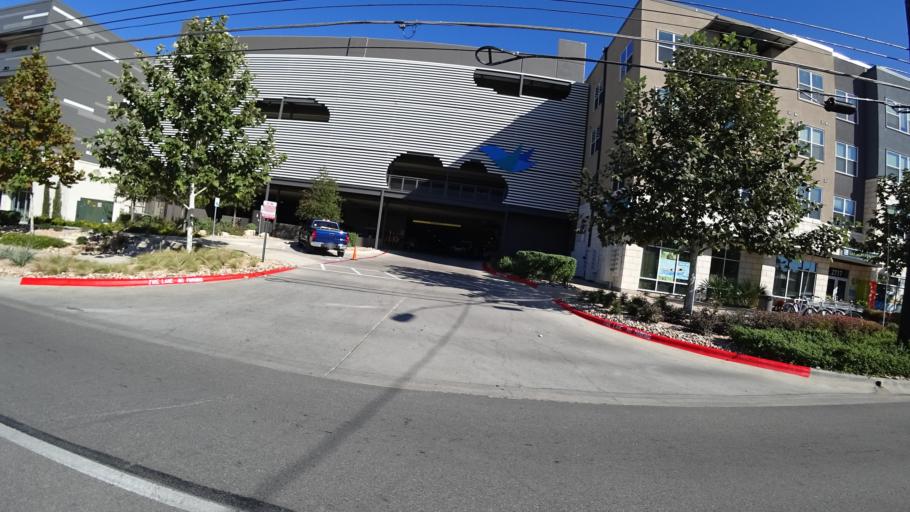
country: US
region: Texas
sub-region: Travis County
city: Rollingwood
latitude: 30.2434
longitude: -97.7815
